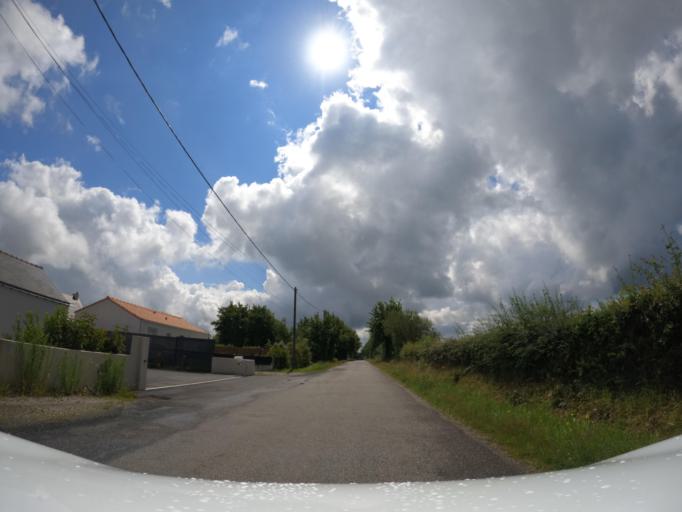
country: FR
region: Pays de la Loire
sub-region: Departement de la Loire-Atlantique
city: Saint-Mars-du-Desert
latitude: 47.3828
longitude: -1.3920
